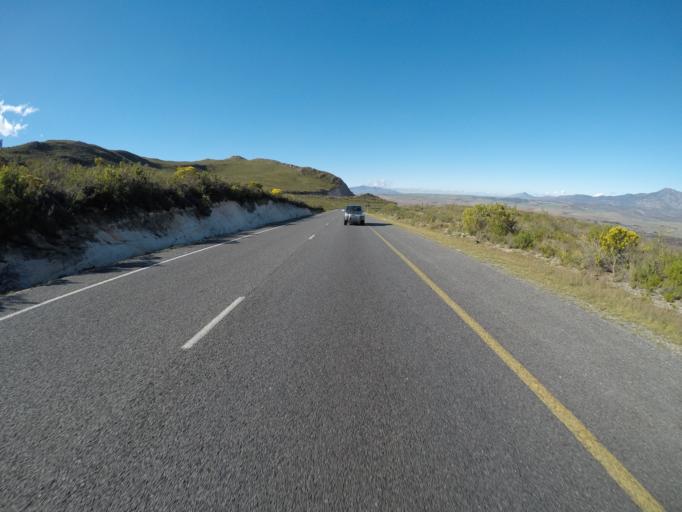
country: ZA
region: Western Cape
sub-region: Overberg District Municipality
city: Grabouw
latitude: -34.2223
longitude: 19.1766
